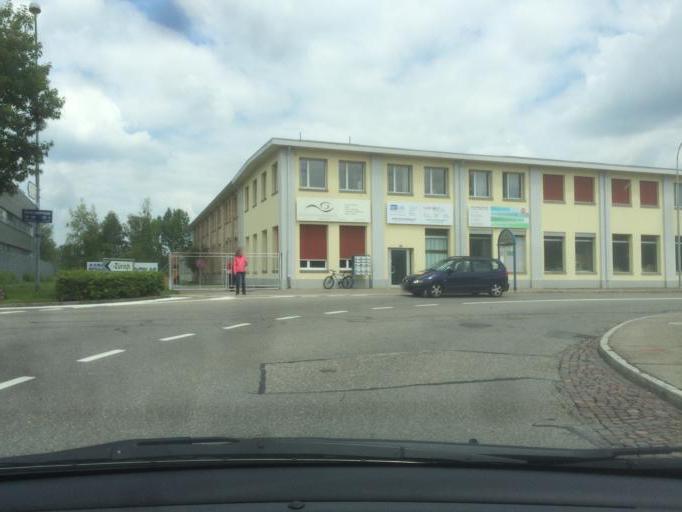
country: CH
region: Zurich
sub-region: Bezirk Hinwil
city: Wetzikon / Robenhausen
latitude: 47.3321
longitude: 8.7915
